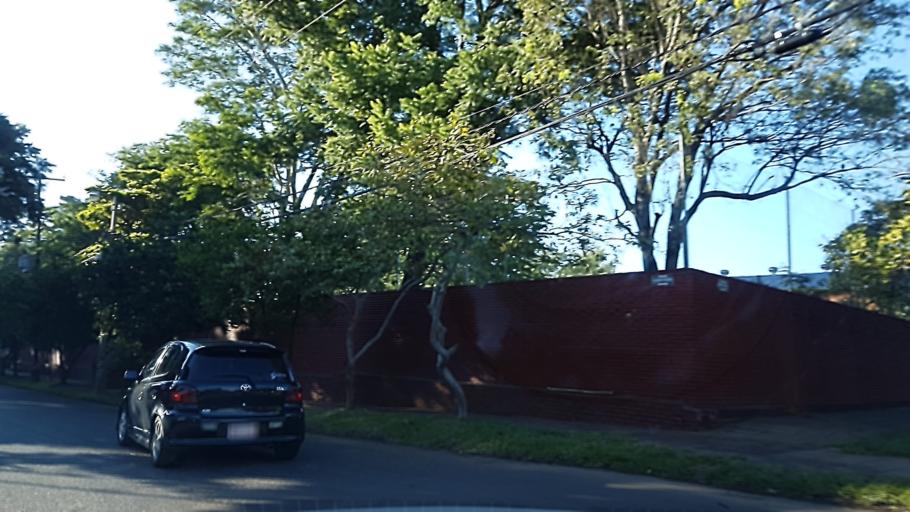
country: PY
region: Central
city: Fernando de la Mora
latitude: -25.2751
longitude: -57.5604
